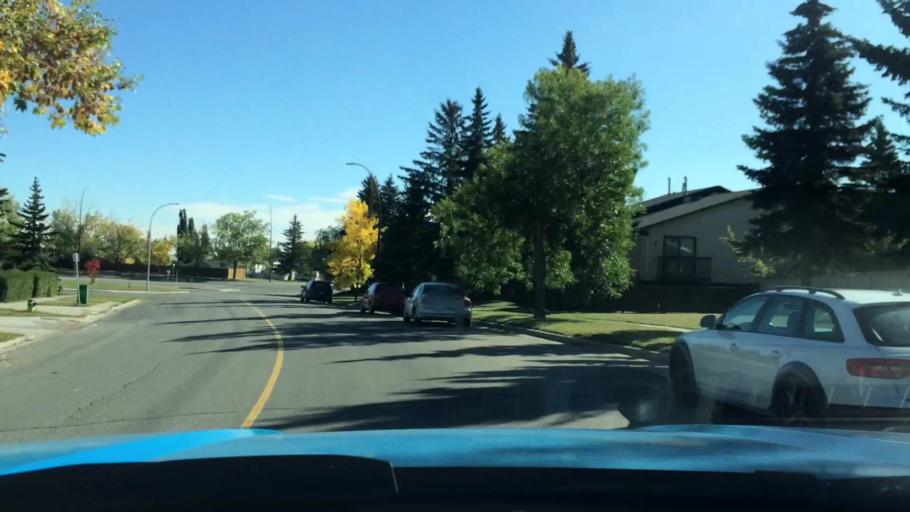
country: CA
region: Alberta
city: Calgary
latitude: 51.1178
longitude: -114.0546
